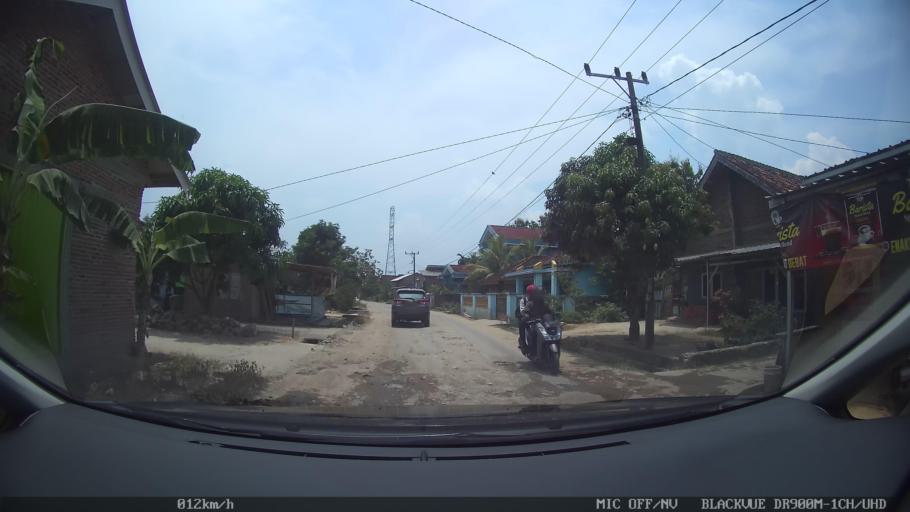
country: ID
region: Lampung
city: Kedaton
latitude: -5.3358
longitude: 105.2473
